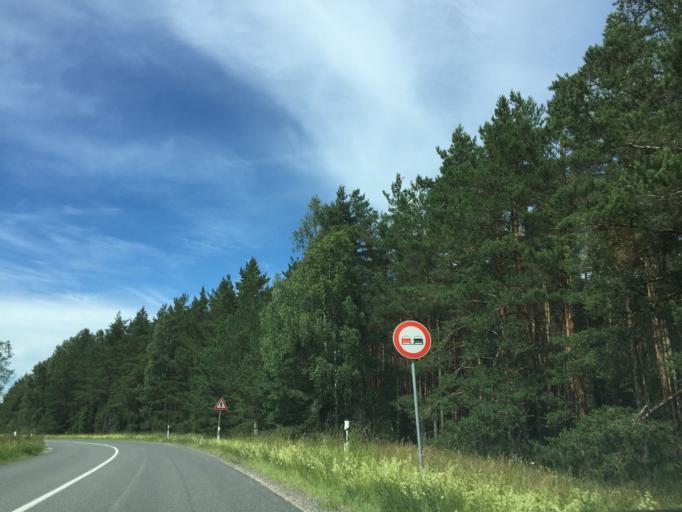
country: LV
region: Dundaga
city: Dundaga
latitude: 57.6277
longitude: 22.5757
